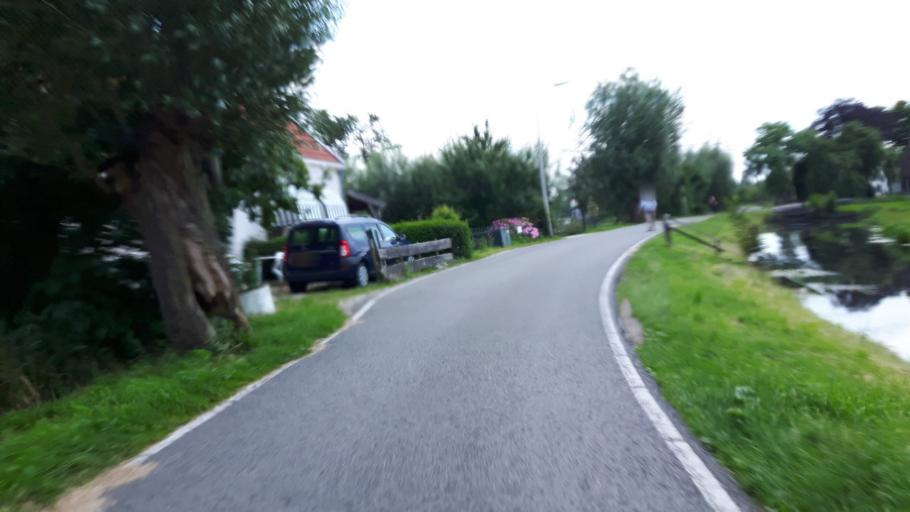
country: NL
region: South Holland
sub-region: Bodegraven-Reeuwijk
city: Bodegraven
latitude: 52.0758
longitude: 4.7343
